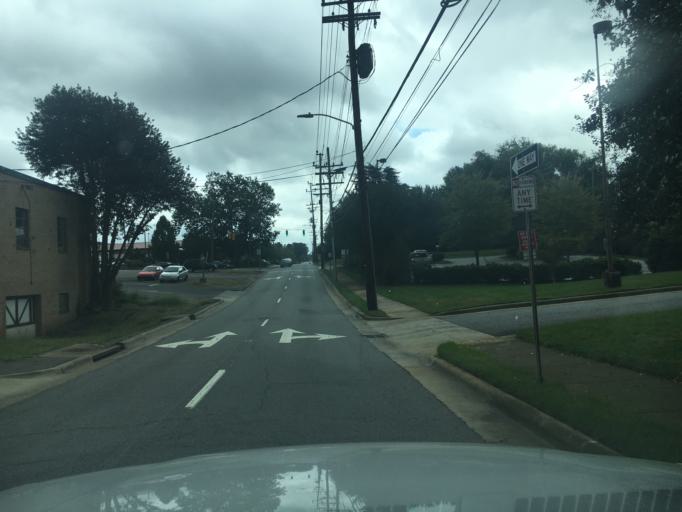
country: US
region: North Carolina
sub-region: Catawba County
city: Hickory
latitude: 35.7301
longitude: -81.3431
